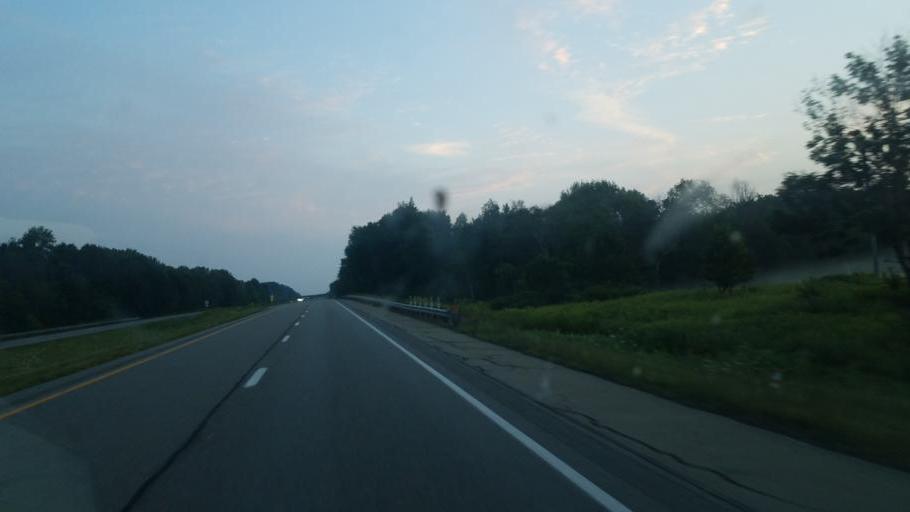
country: US
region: Pennsylvania
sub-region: Crawford County
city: Cochranton
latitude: 41.4749
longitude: -80.1668
